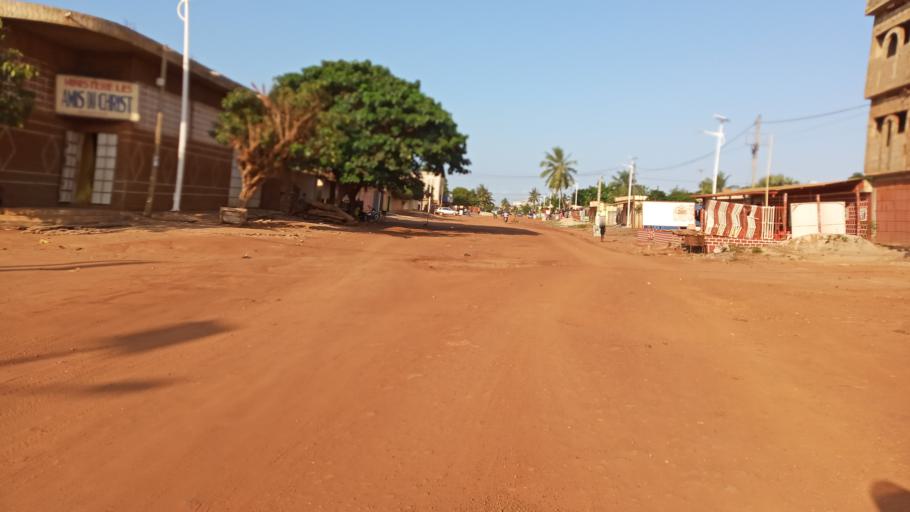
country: TG
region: Maritime
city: Lome
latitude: 6.1965
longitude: 1.1910
